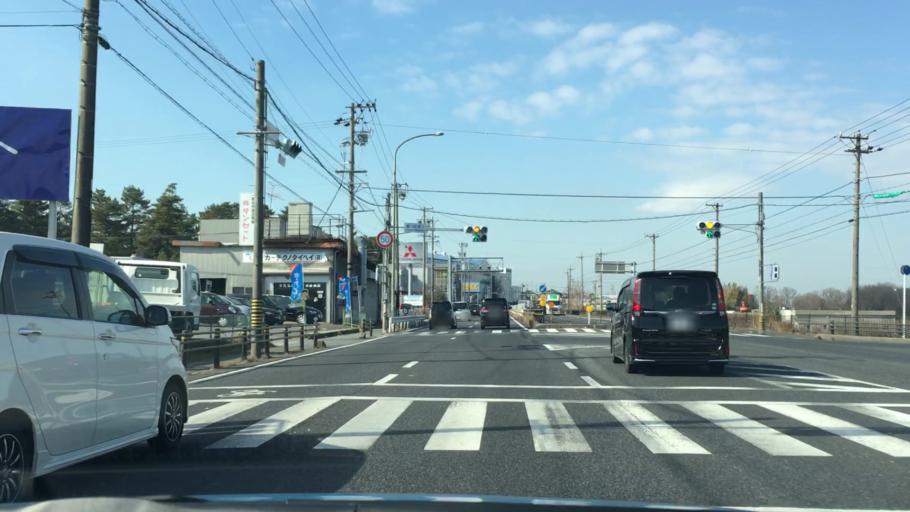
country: JP
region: Aichi
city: Okazaki
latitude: 34.9168
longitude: 137.2125
